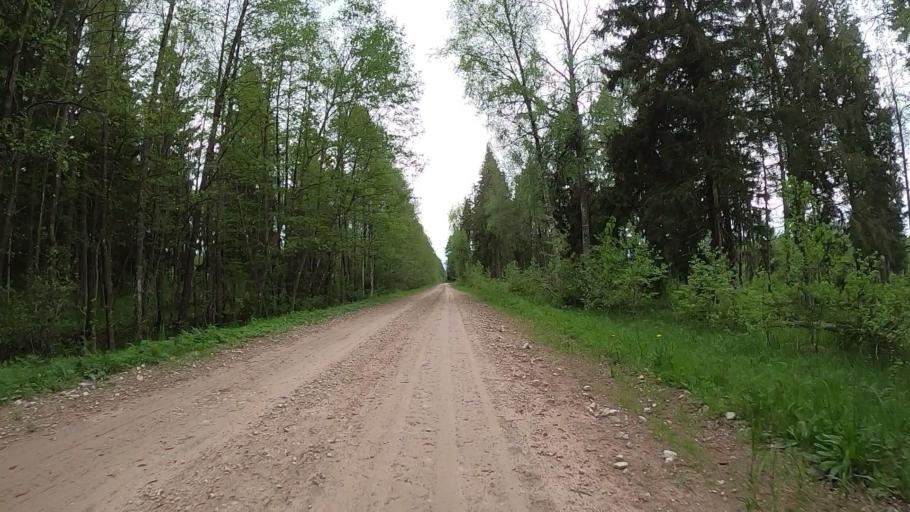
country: LV
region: Ozolnieku
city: Ozolnieki
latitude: 56.7761
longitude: 23.7674
